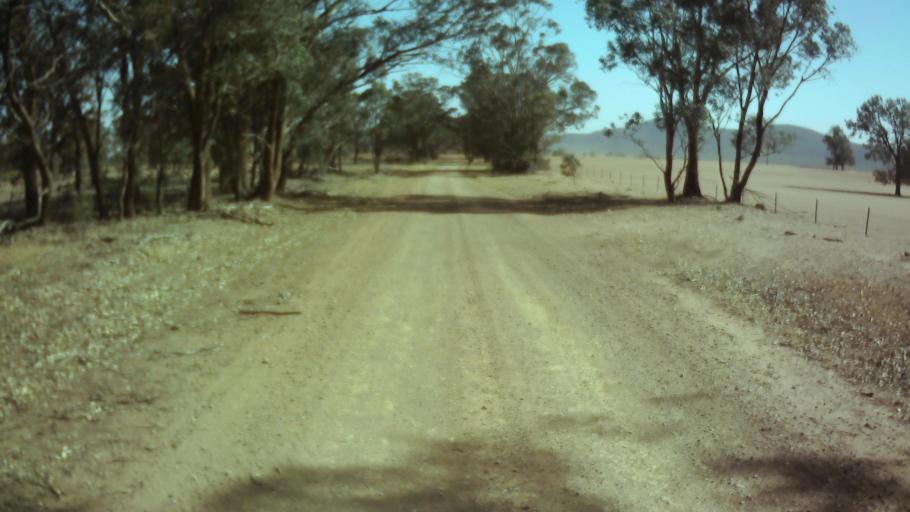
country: AU
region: New South Wales
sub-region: Weddin
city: Grenfell
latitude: -33.8446
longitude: 148.0174
